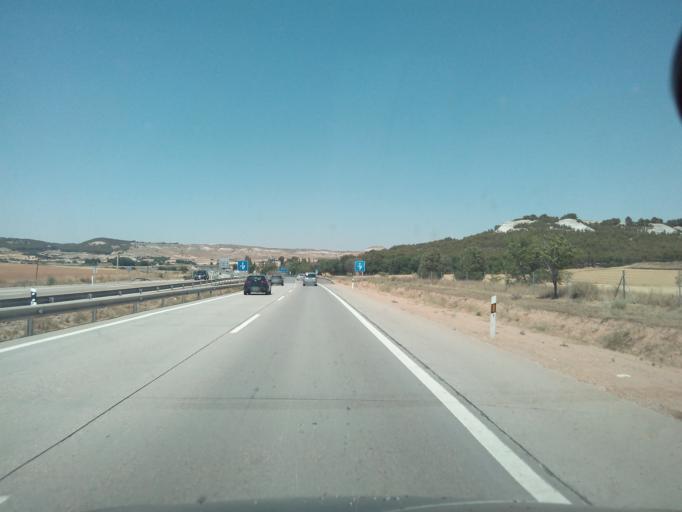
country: ES
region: Castille-La Mancha
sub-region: Province of Toledo
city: Dosbarrios
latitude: 39.7973
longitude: -3.4799
